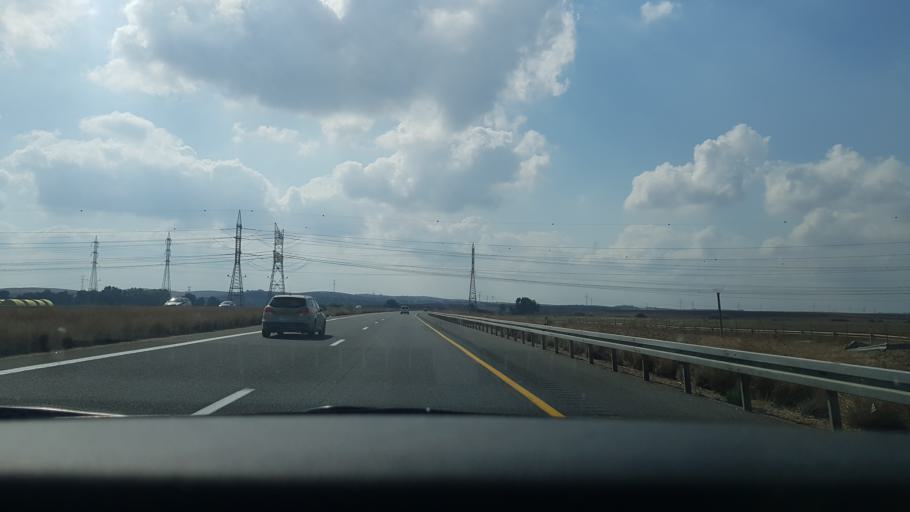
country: IL
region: Central District
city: Bene 'Ayish
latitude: 31.7146
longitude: 34.8203
